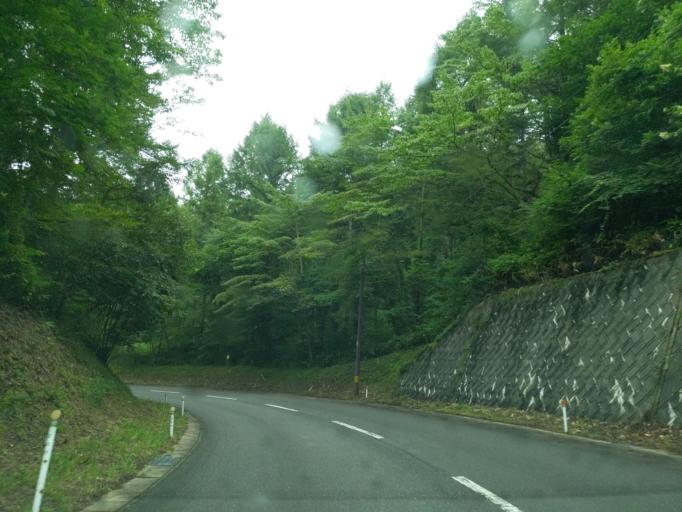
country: JP
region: Fukushima
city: Sukagawa
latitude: 37.2606
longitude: 140.0964
